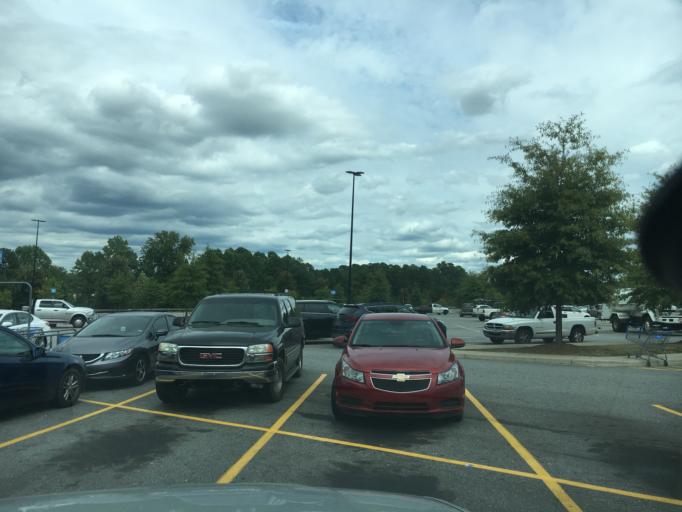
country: US
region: South Carolina
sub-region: Laurens County
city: Watts Mills
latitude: 34.4905
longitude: -81.9837
